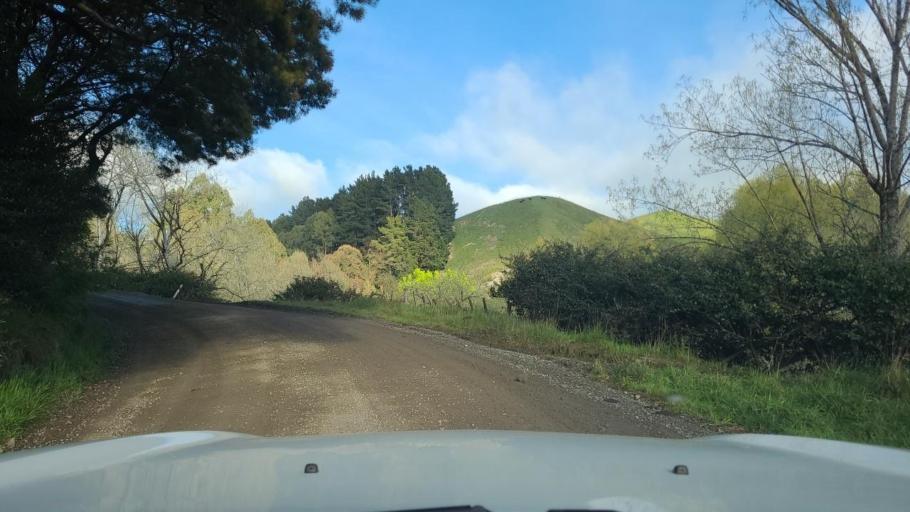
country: NZ
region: Wellington
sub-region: Masterton District
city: Masterton
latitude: -41.1971
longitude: 175.6705
